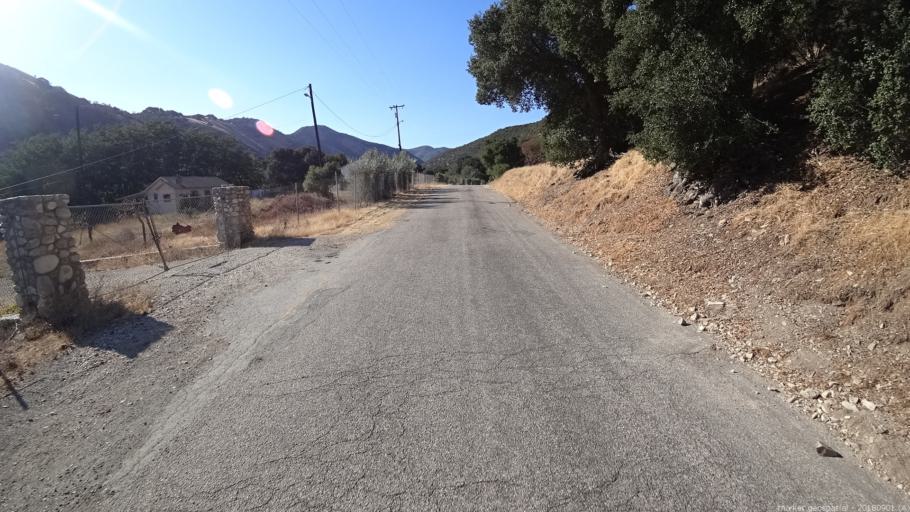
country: US
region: California
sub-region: Monterey County
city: Greenfield
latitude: 36.2119
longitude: -121.2798
